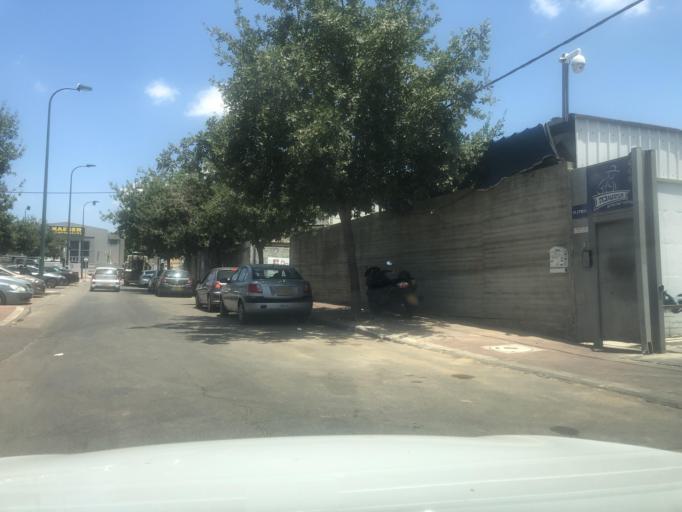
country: IL
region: Central District
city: Kfar Saba
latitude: 32.1548
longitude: 34.9210
